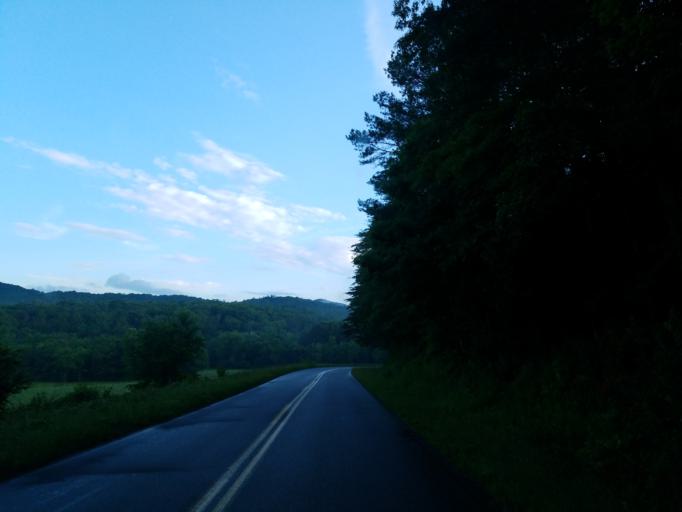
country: US
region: Georgia
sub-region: Fannin County
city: Blue Ridge
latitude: 34.7387
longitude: -84.2273
